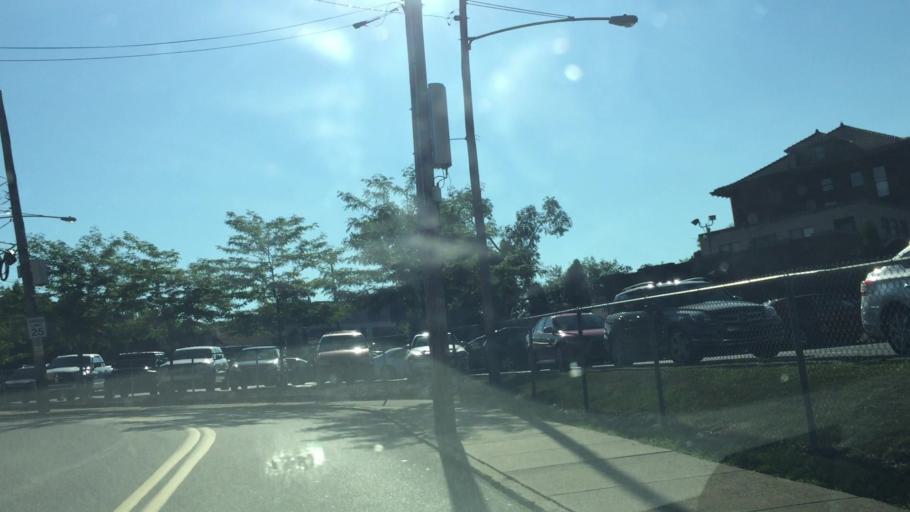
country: US
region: Pennsylvania
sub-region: Allegheny County
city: Bloomfield
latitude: 40.4403
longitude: -79.9647
